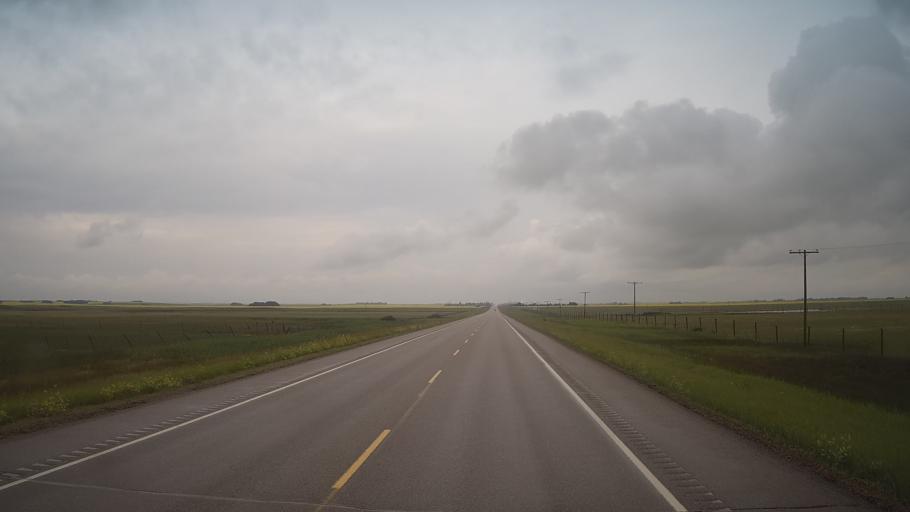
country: CA
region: Saskatchewan
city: Unity
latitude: 52.4349
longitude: -108.9880
